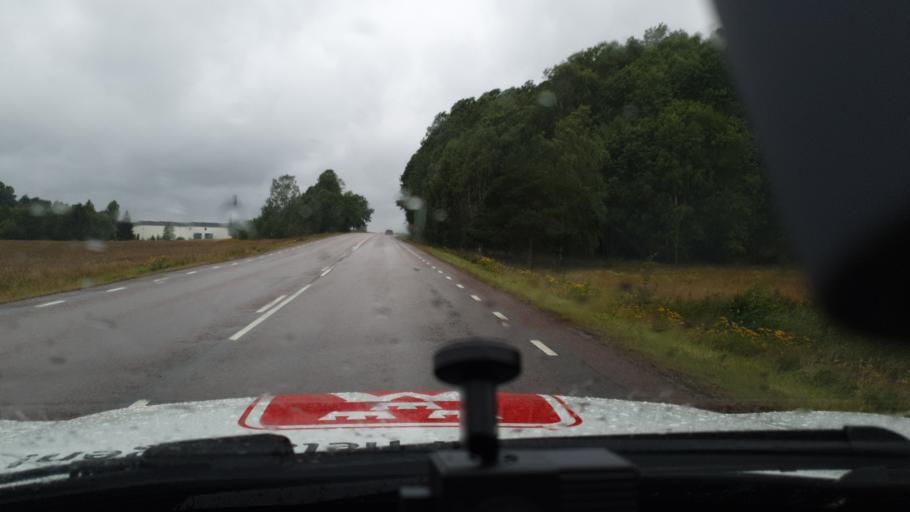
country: SE
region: Vaermland
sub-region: Karlstads Kommun
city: Edsvalla
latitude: 59.4032
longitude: 13.2234
